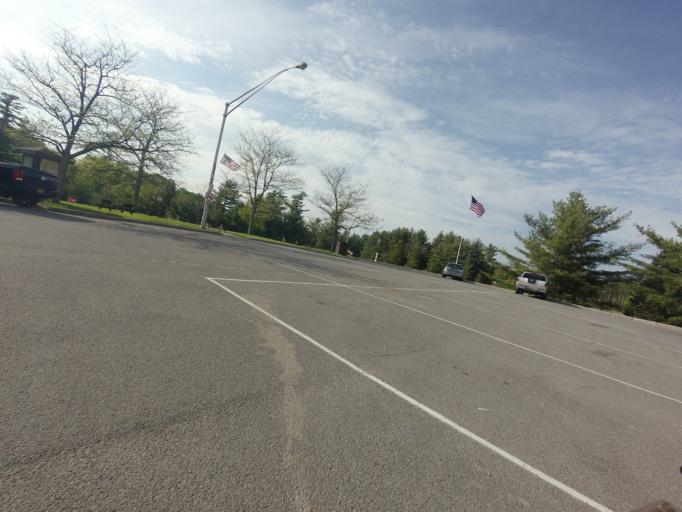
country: US
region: New York
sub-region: St. Lawrence County
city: Gouverneur
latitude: 44.1490
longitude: -75.3164
